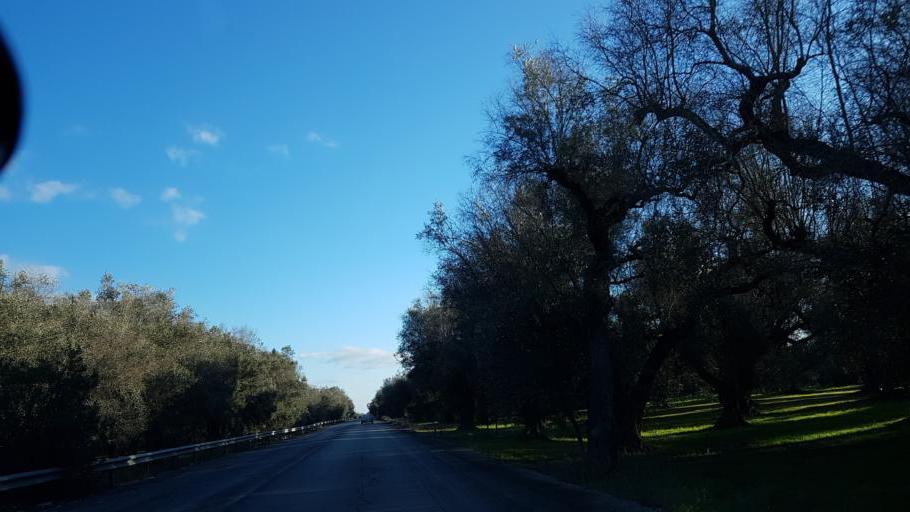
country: IT
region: Apulia
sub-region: Provincia di Brindisi
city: San Pietro Vernotico
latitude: 40.4667
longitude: 18.0159
